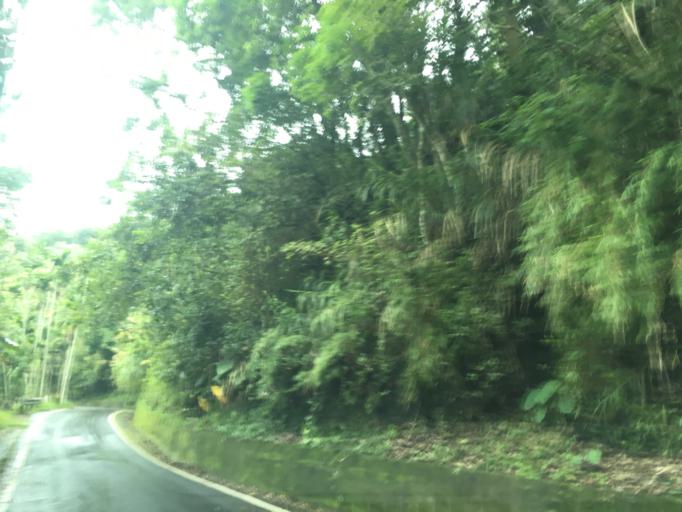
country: TW
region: Taiwan
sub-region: Yunlin
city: Douliu
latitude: 23.5583
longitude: 120.6556
